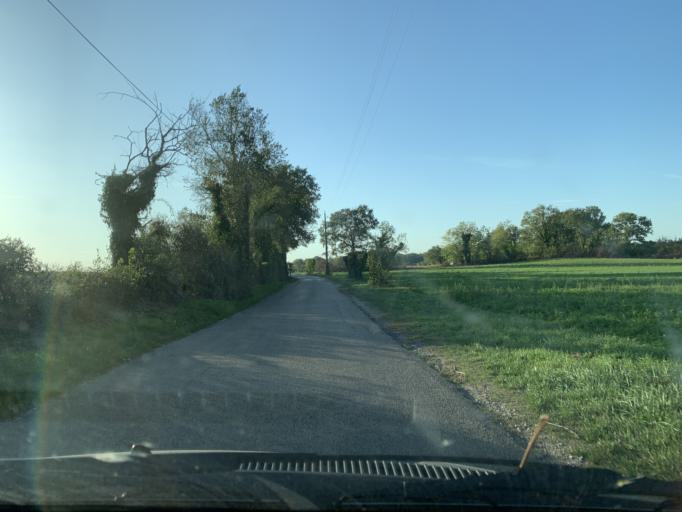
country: FR
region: Rhone-Alpes
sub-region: Departement de l'Ain
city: Saint-Jean-de-Niost
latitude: 45.8383
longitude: 5.2099
